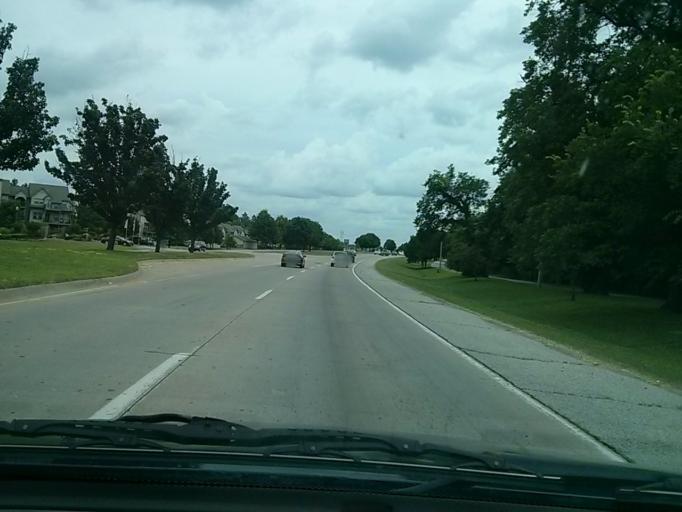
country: US
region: Oklahoma
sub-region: Tulsa County
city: Jenks
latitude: 36.0306
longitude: -95.9531
